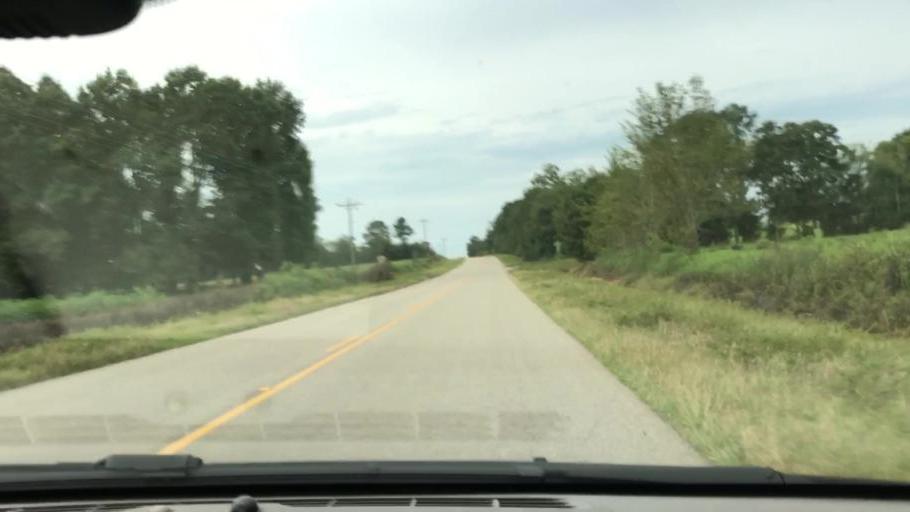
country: US
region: Alabama
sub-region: Houston County
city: Ashford
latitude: 31.2249
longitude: -85.1846
